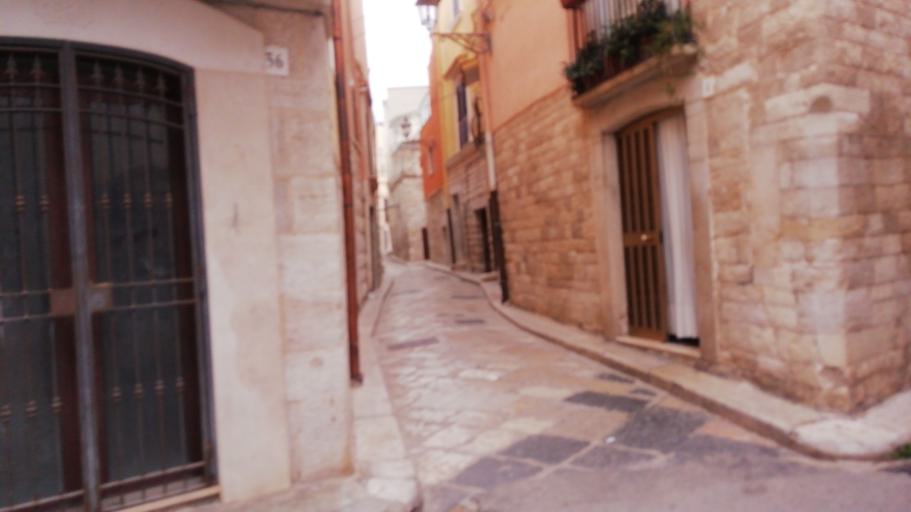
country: IT
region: Apulia
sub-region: Provincia di Barletta - Andria - Trani
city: Andria
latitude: 41.2243
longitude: 16.2968
